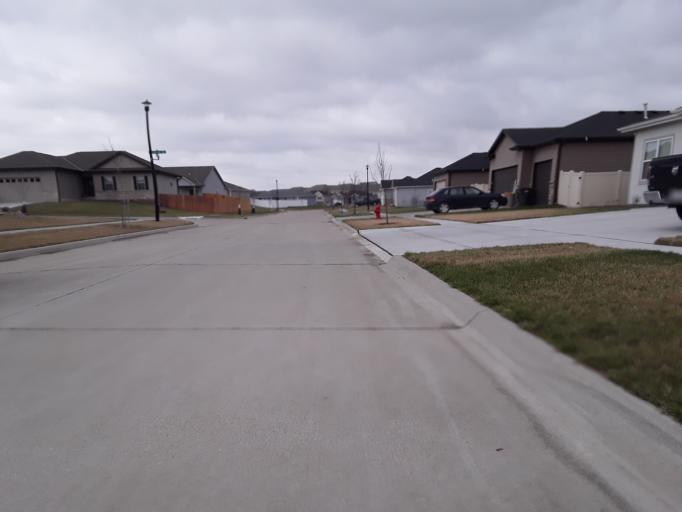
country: US
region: Nebraska
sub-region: Lancaster County
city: Lincoln
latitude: 40.8468
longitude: -96.5970
